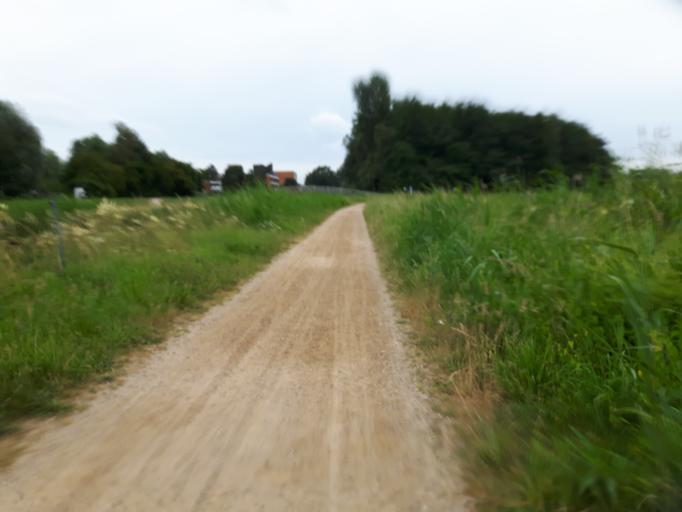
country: DE
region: Lower Saxony
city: Winsen
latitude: 53.3546
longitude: 10.1990
